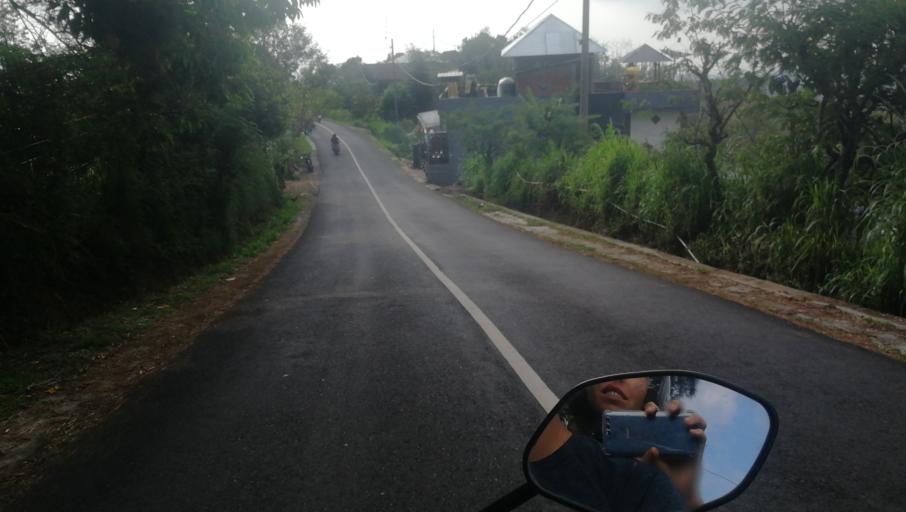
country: ID
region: Bali
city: Munduk
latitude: -8.2602
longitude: 115.0829
